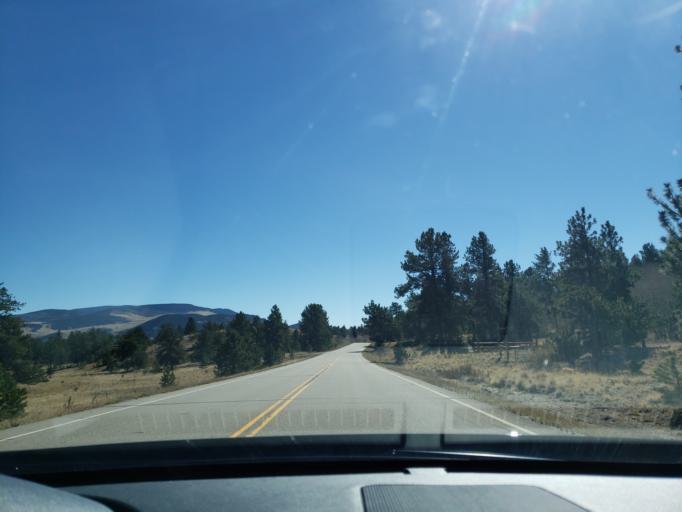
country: US
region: Colorado
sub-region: Chaffee County
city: Buena Vista
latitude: 38.8893
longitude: -105.6848
